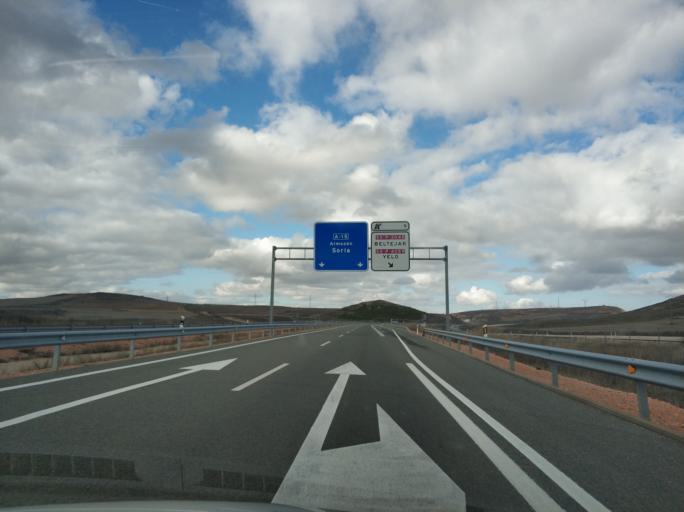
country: ES
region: Castille and Leon
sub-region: Provincia de Soria
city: Yelo
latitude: 41.2141
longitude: -2.4681
